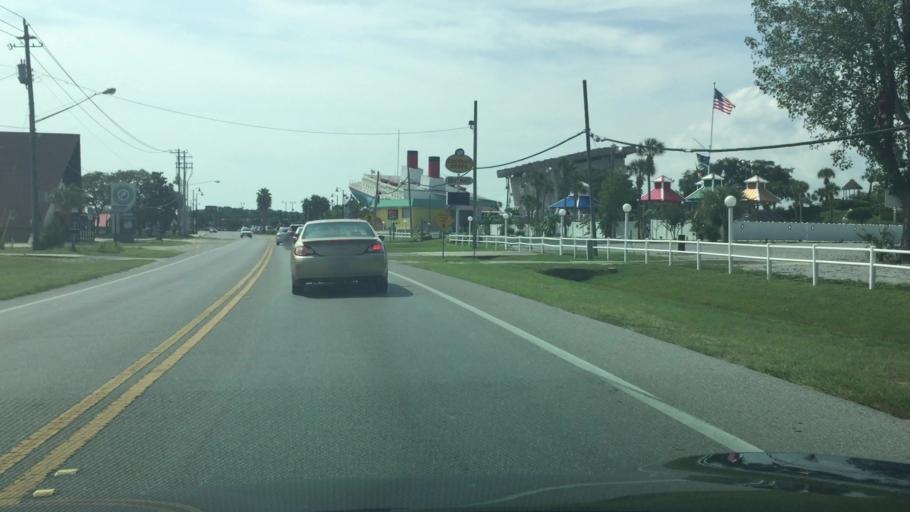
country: US
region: Florida
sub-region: Bay County
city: Panama City Beach
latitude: 30.1770
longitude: -85.7974
